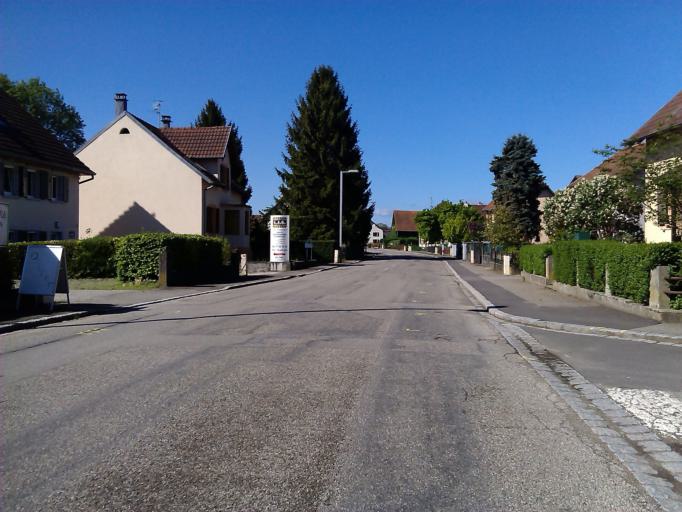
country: FR
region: Alsace
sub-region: Departement du Haut-Rhin
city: Aspach
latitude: 47.6795
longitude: 7.2164
